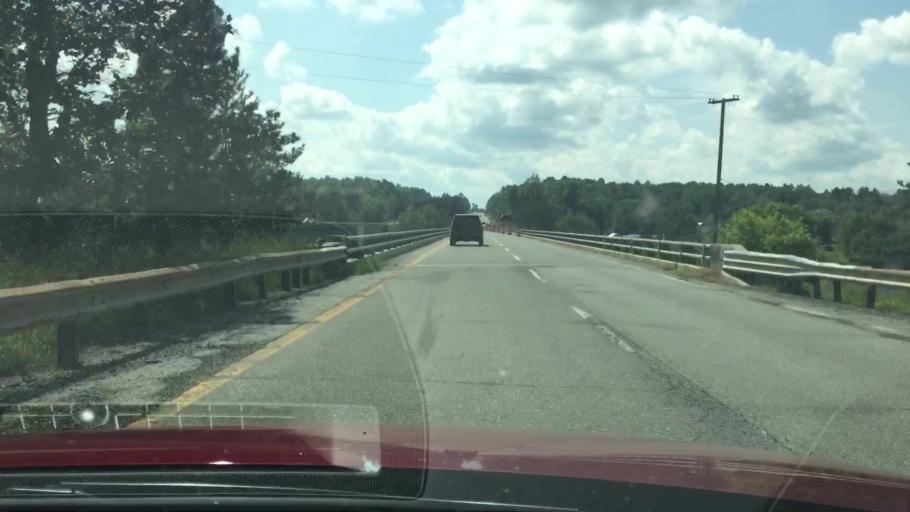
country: US
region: Maine
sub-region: Penobscot County
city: Medway
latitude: 45.6037
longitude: -68.5270
